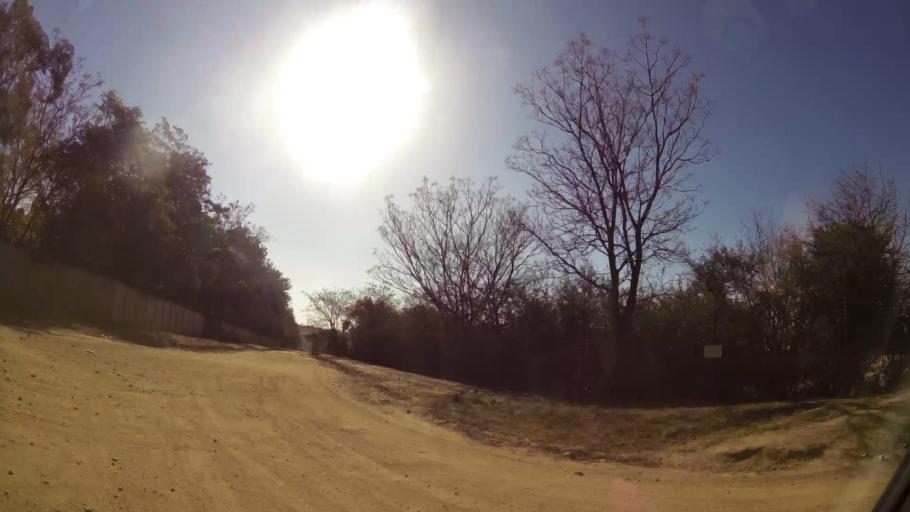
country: ZA
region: Gauteng
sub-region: City of Johannesburg Metropolitan Municipality
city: Diepsloot
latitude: -26.0096
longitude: 27.9594
